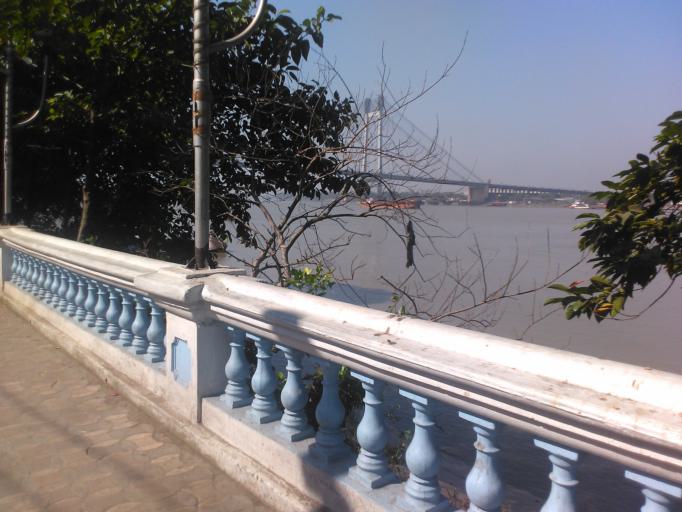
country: IN
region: West Bengal
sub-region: Kolkata
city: Bara Bazar
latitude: 22.5598
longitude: 88.3333
